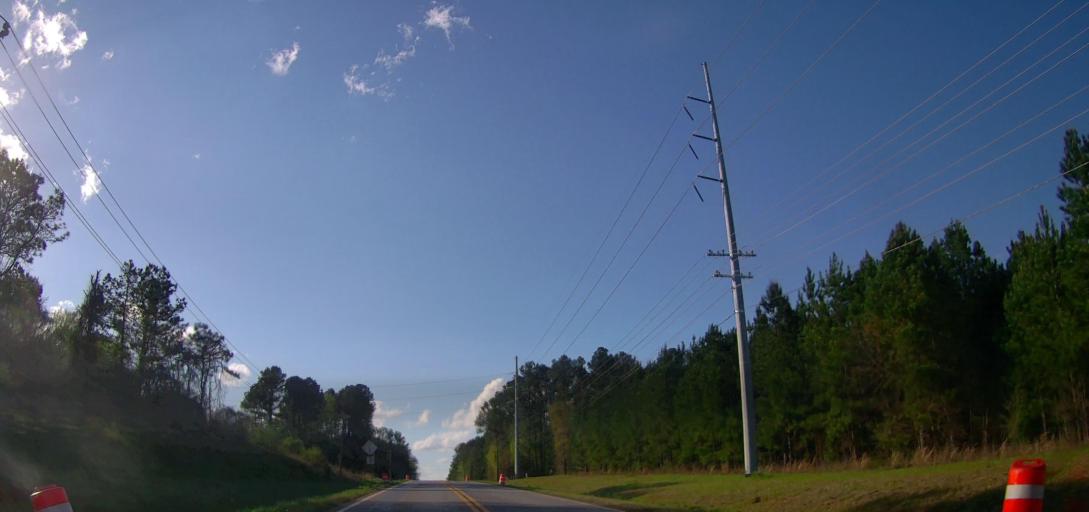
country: US
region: Georgia
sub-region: Baldwin County
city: Milledgeville
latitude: 33.1547
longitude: -83.3484
